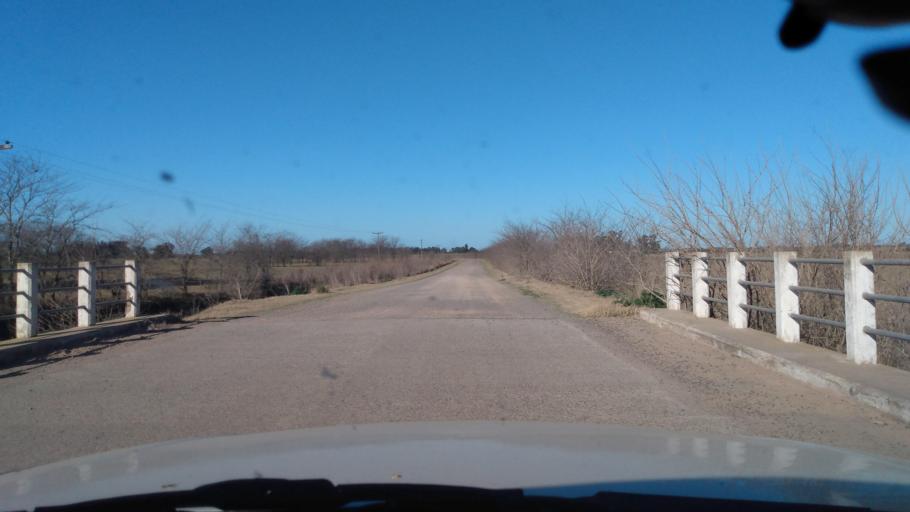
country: AR
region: Buenos Aires
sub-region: Partido de Mercedes
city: Mercedes
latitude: -34.6120
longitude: -59.3247
